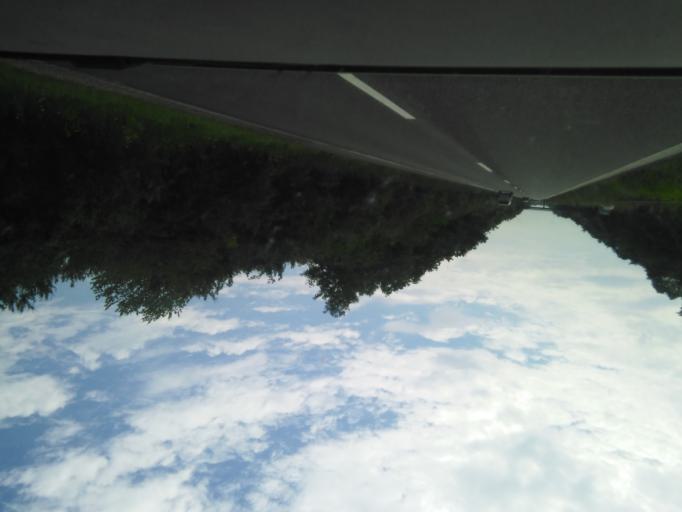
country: DK
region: Zealand
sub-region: Slagelse Kommune
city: Forlev
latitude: 55.3658
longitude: 11.2646
